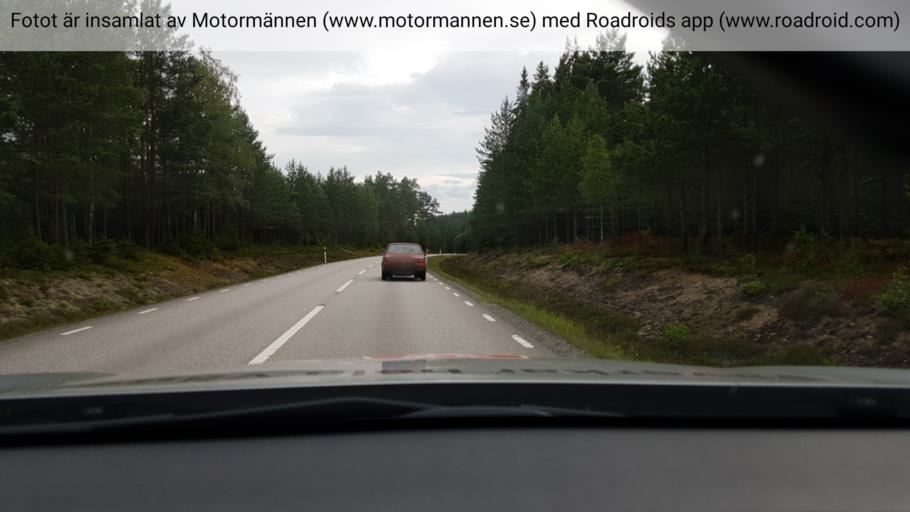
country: SE
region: Vaestra Goetaland
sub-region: Bengtsfors Kommun
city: Dals Langed
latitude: 58.8958
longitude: 12.2142
